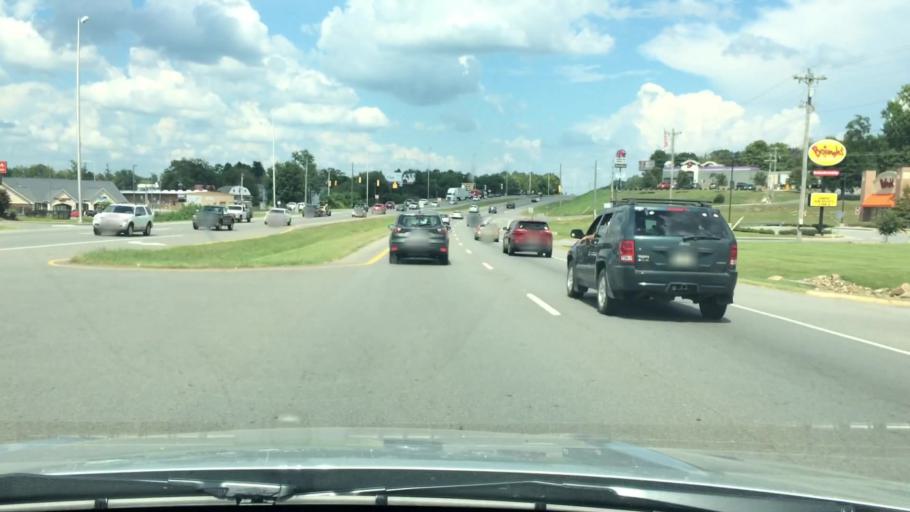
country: US
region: Tennessee
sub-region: Monroe County
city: Madisonville
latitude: 35.5159
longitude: -84.3602
